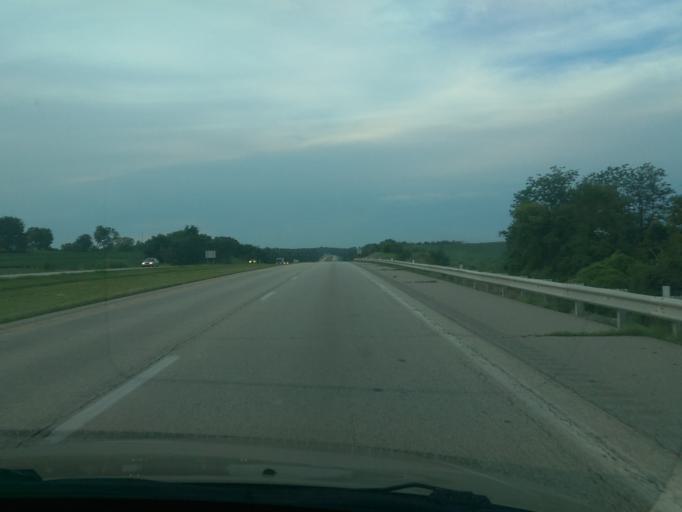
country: US
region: Missouri
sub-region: Andrew County
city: Country Club Village
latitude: 39.8290
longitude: -94.8052
